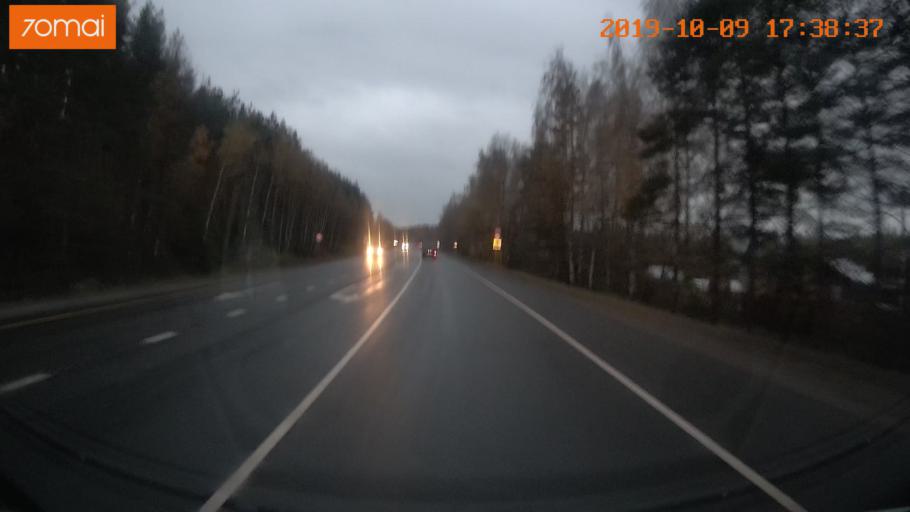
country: RU
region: Ivanovo
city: Bogorodskoye
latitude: 57.0694
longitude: 40.9515
